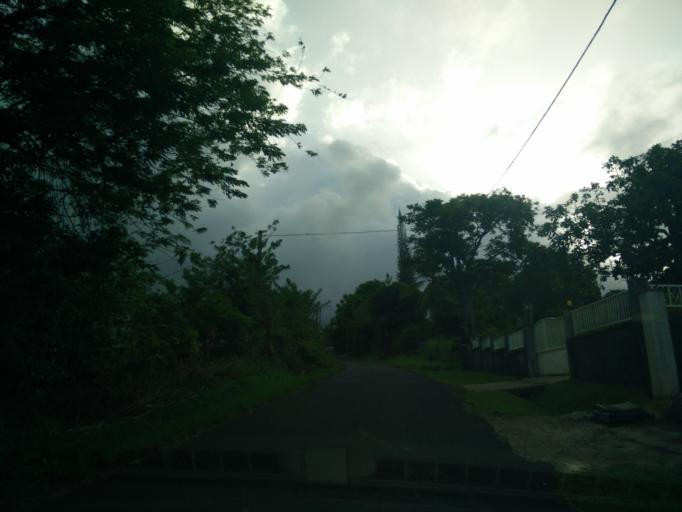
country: GP
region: Guadeloupe
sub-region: Guadeloupe
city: Petit-Bourg
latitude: 16.1803
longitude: -61.6118
